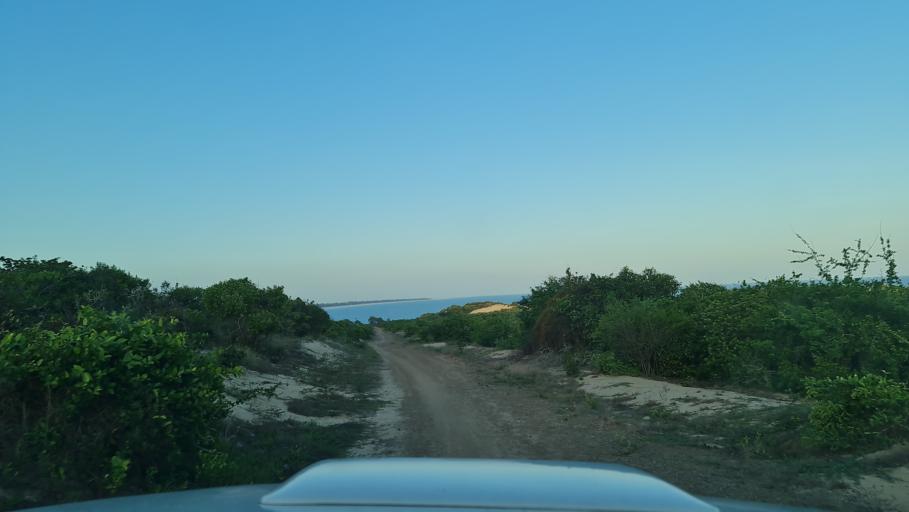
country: MZ
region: Nampula
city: Ilha de Mocambique
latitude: -15.6318
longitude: 40.4190
